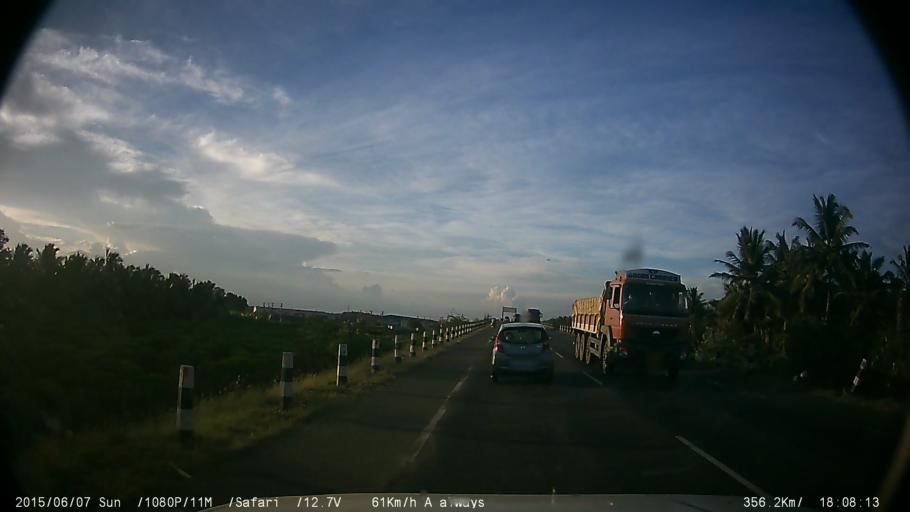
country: IN
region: Tamil Nadu
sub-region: Coimbatore
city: Irugur
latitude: 11.0197
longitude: 77.0749
